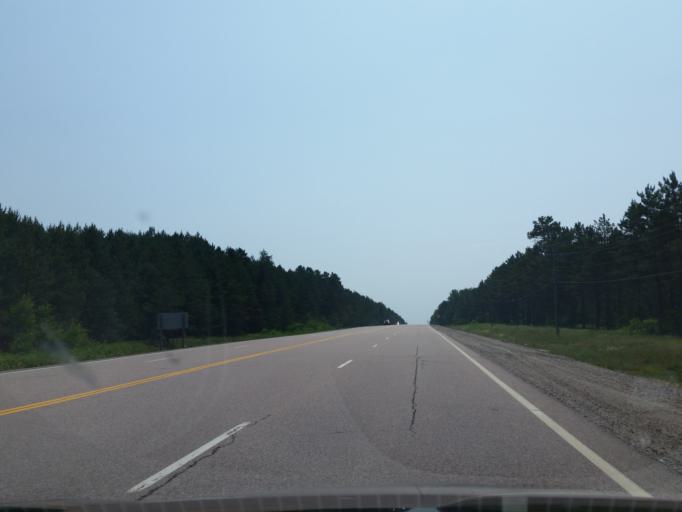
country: CA
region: Ontario
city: Deep River
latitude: 46.1778
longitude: -77.8391
